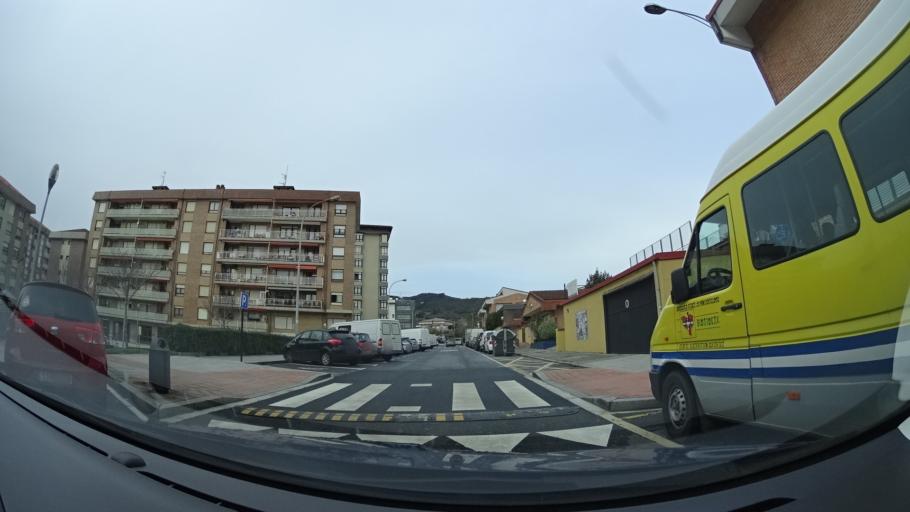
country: ES
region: Basque Country
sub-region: Bizkaia
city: Bermeo
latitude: 43.4215
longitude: -2.7272
